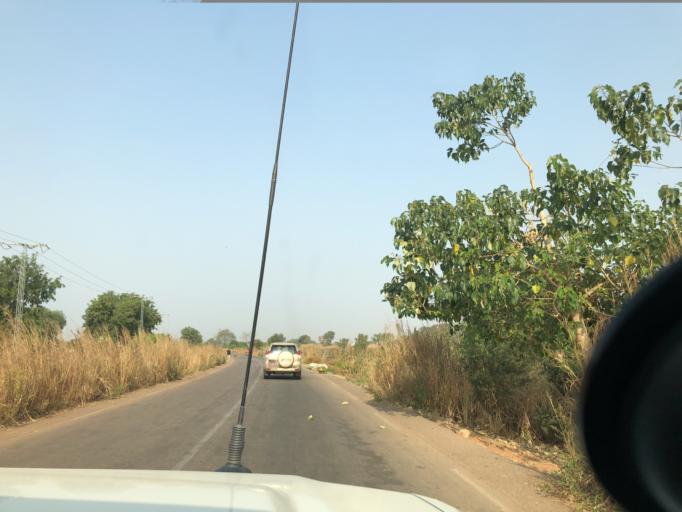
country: TD
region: Logone Occidental
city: Moundou
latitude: 8.5804
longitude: 16.0325
